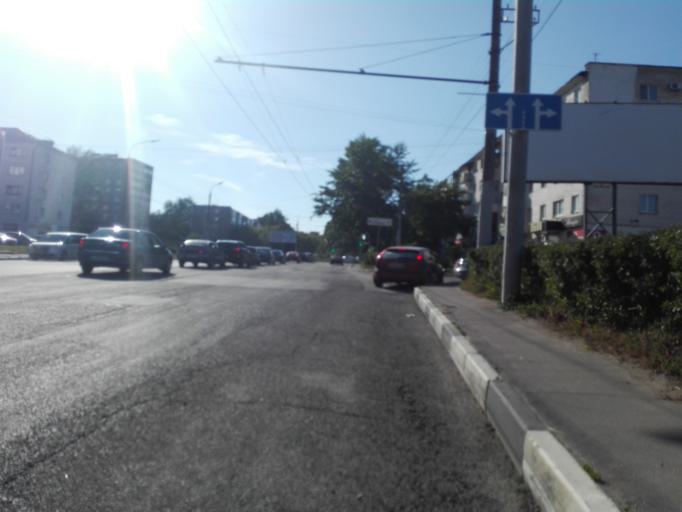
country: RU
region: Orjol
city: Orel
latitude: 52.9808
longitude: 36.0713
